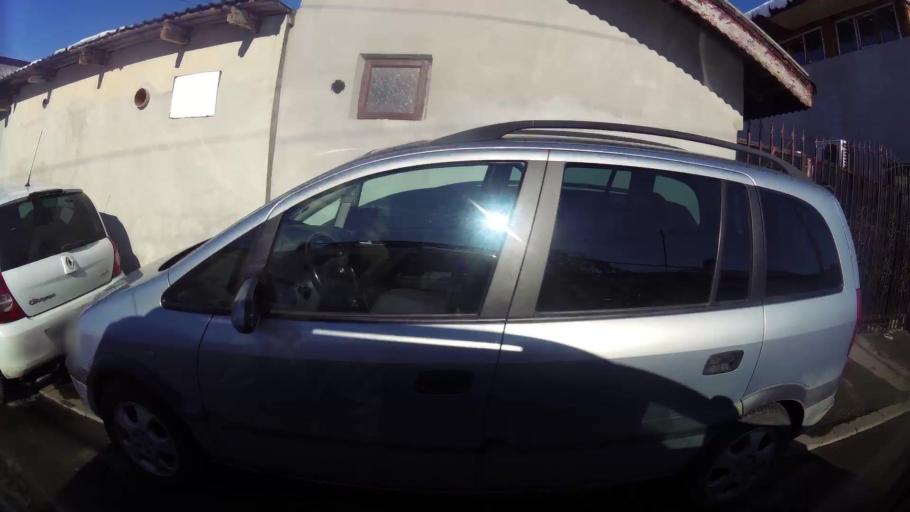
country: RO
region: Ilfov
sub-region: Comuna Magurele
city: Magurele
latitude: 44.3968
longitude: 26.0502
